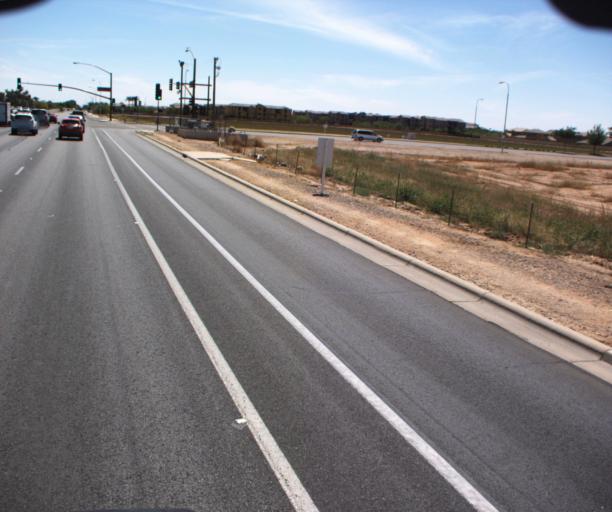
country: US
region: Arizona
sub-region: Maricopa County
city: Chandler
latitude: 33.2630
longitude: -111.8415
